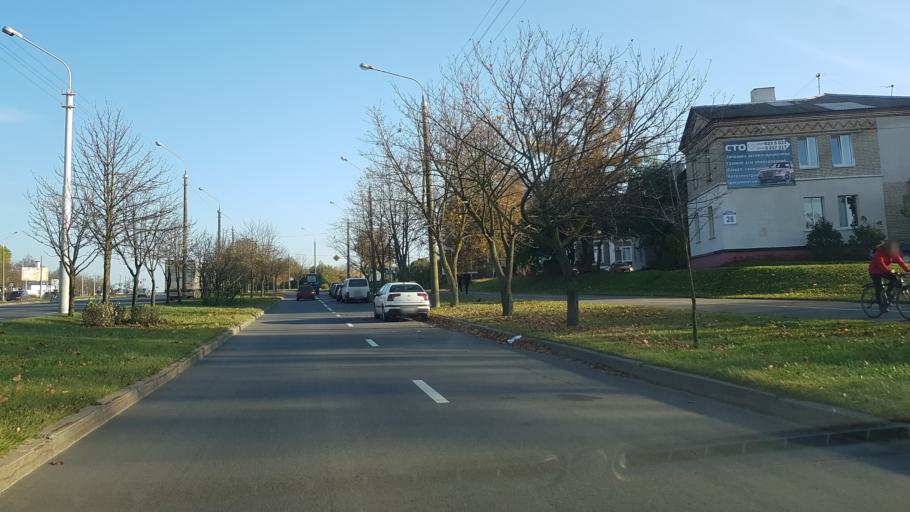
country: BY
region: Minsk
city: Syenitsa
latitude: 53.8811
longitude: 27.5079
